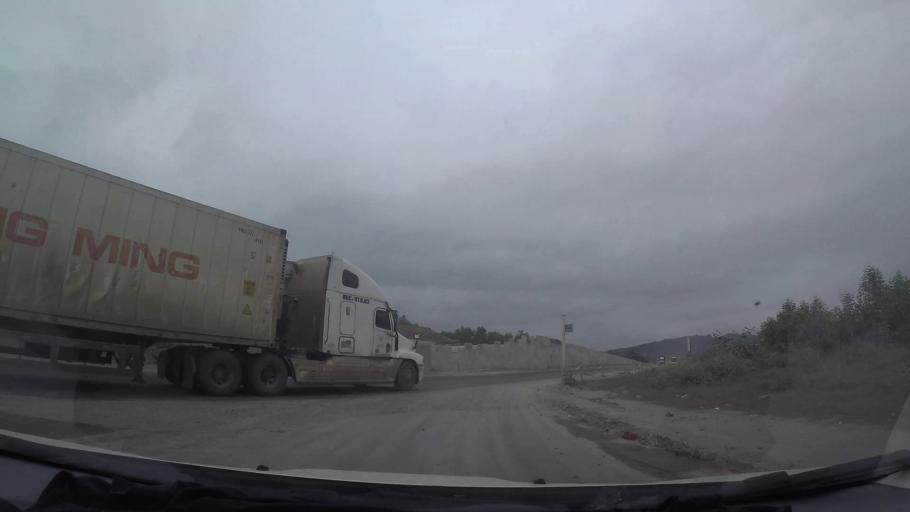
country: VN
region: Da Nang
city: Lien Chieu
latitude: 16.0928
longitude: 108.0868
